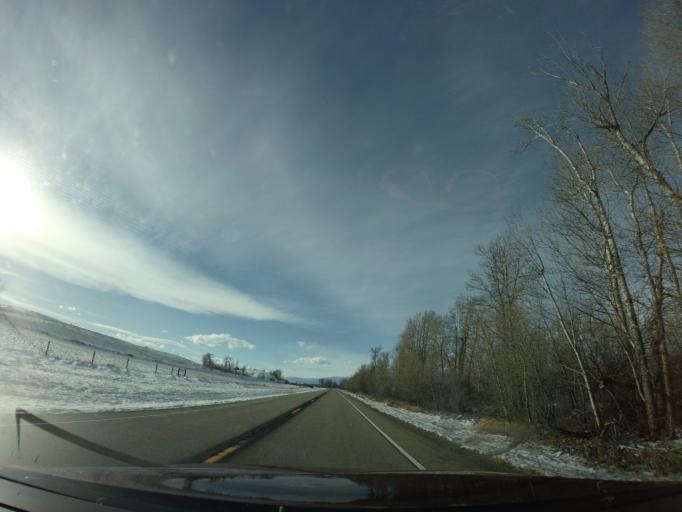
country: US
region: Montana
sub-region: Carbon County
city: Red Lodge
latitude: 45.4098
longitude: -109.1196
